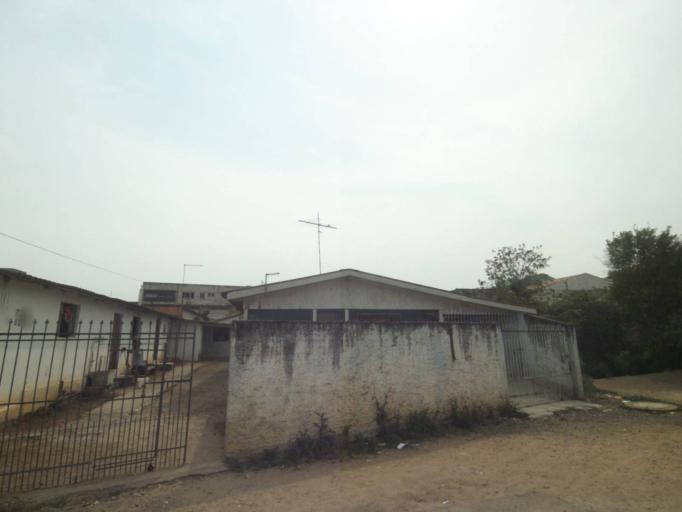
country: BR
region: Parana
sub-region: Sao Jose Dos Pinhais
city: Sao Jose dos Pinhais
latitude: -25.5208
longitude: -49.2845
